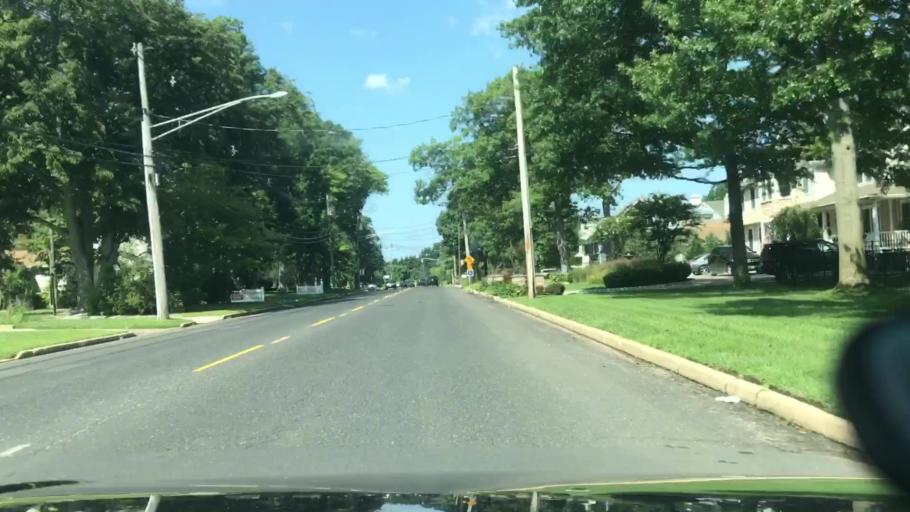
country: US
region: New Jersey
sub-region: Monmouth County
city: Oceanport
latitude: 40.3221
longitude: -74.0105
